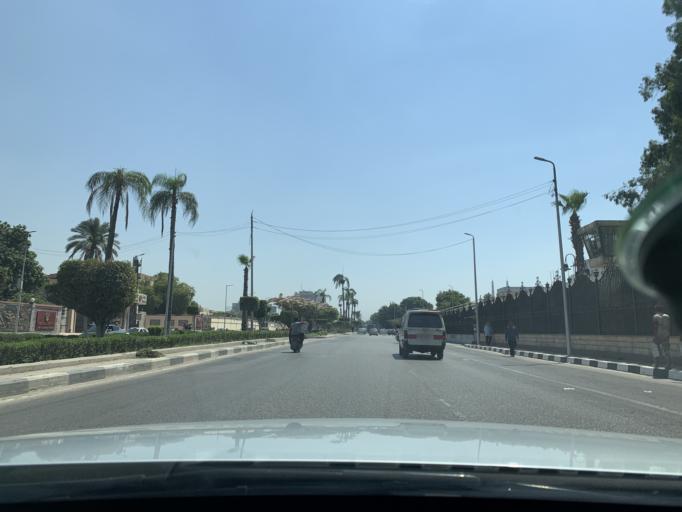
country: EG
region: Muhafazat al Qahirah
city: Cairo
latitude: 30.0807
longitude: 31.2921
